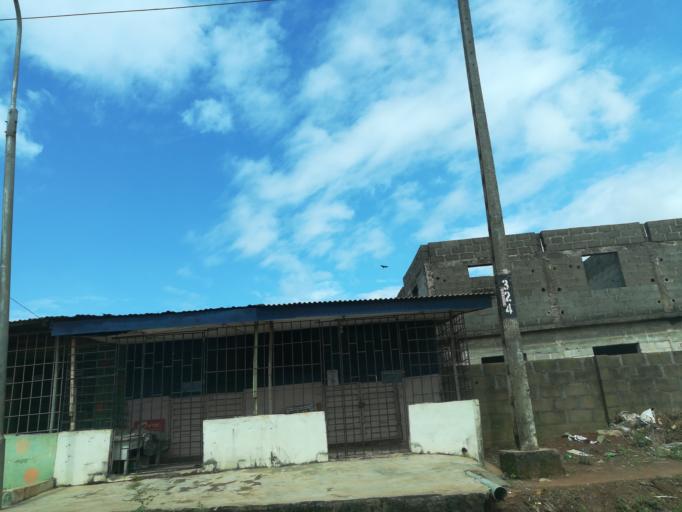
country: NG
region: Lagos
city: Ikorodu
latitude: 6.6026
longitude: 3.5181
